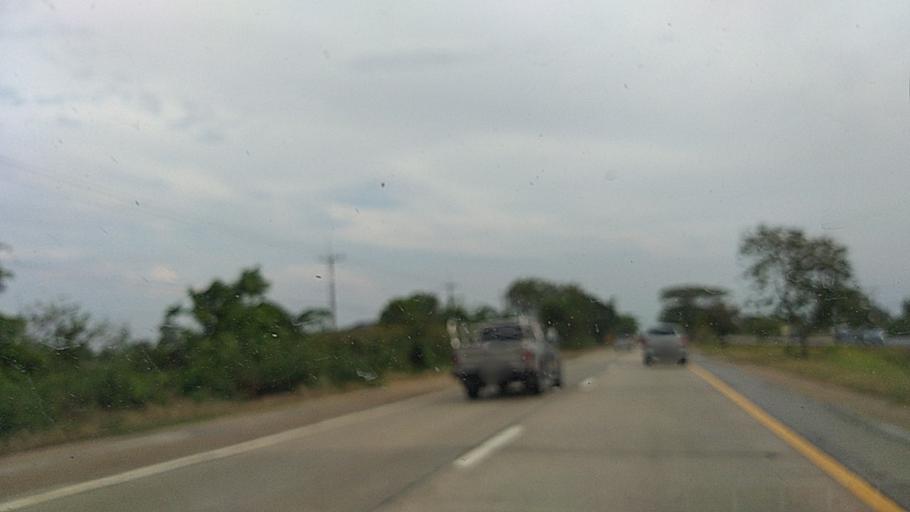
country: TH
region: Phra Nakhon Si Ayutthaya
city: Bang Pa-in
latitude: 14.2343
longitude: 100.5391
